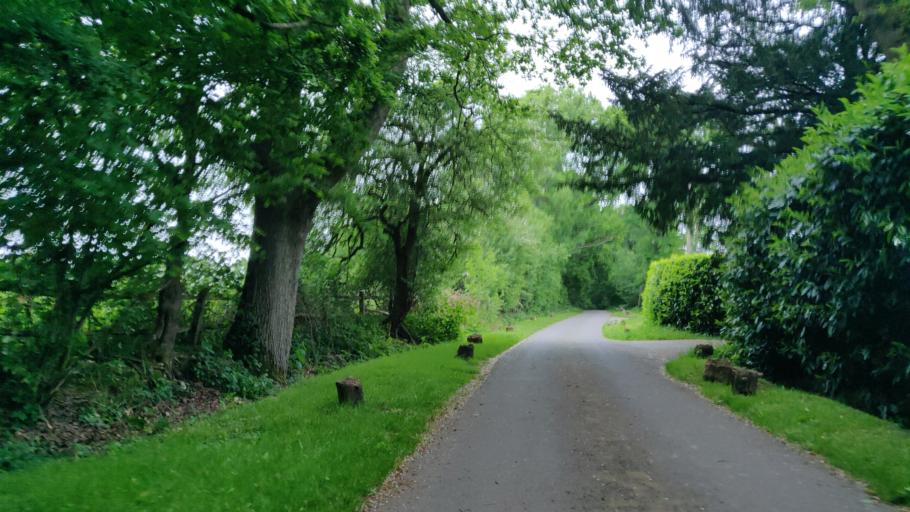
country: GB
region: England
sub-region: West Sussex
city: Southwater
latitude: 51.0198
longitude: -0.3313
